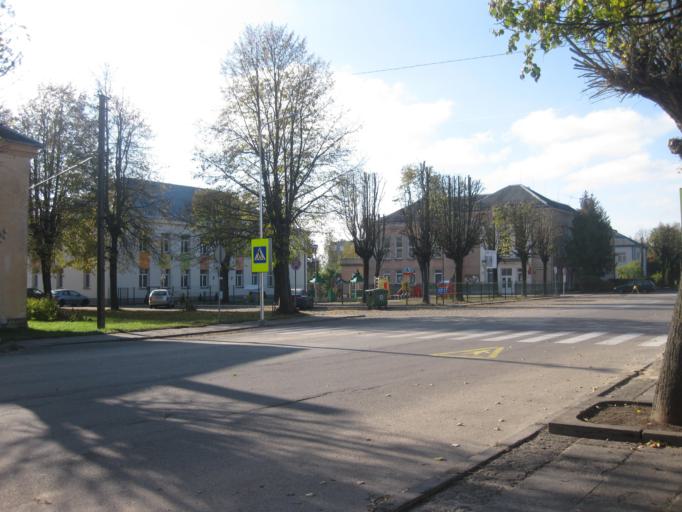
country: LT
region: Kauno apskritis
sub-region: Kauno rajonas
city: Garliava
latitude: 54.8357
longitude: 23.8715
